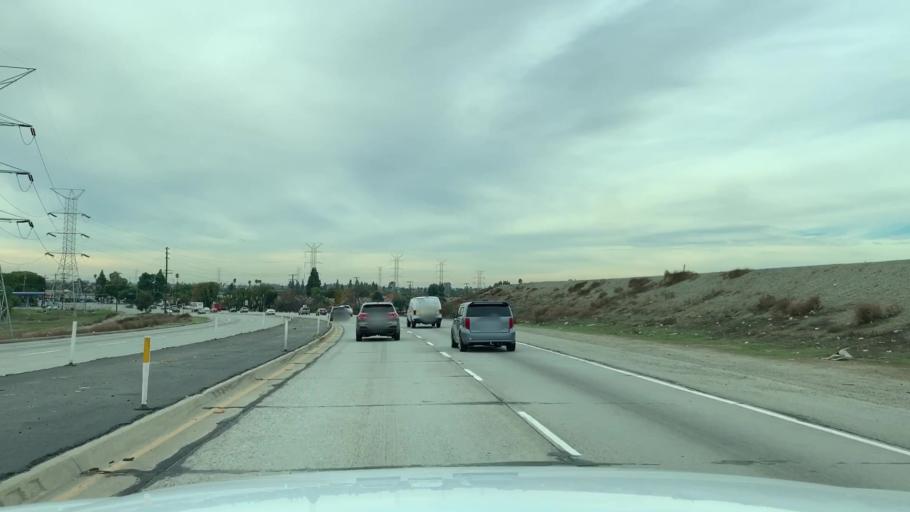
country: US
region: California
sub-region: Los Angeles County
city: Montebello
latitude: 34.0198
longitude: -118.0763
